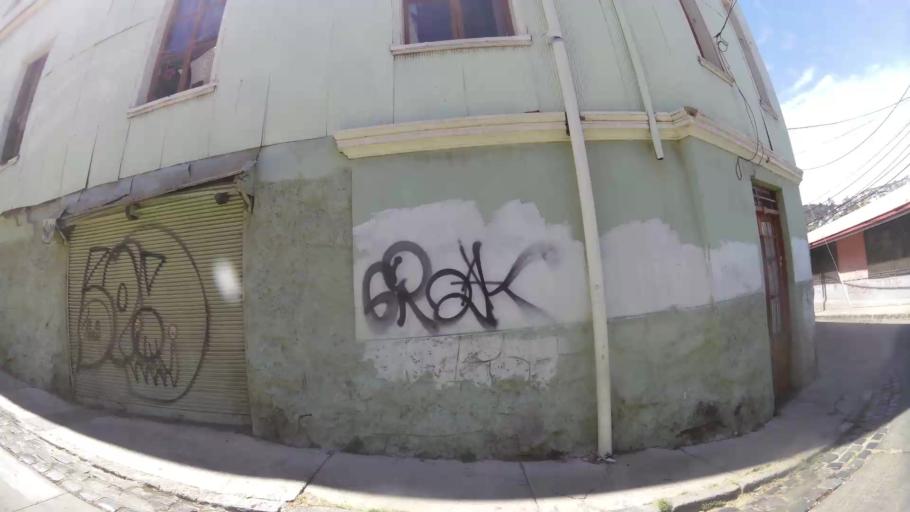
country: CL
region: Valparaiso
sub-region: Provincia de Valparaiso
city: Valparaiso
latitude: -33.0502
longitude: -71.6009
